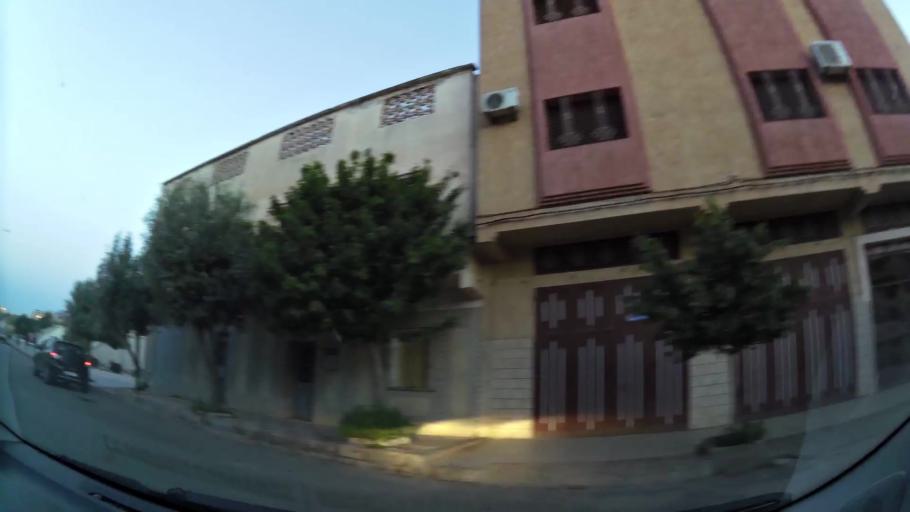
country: MA
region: Oriental
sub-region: Oujda-Angad
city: Oujda
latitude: 34.6968
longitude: -1.9201
